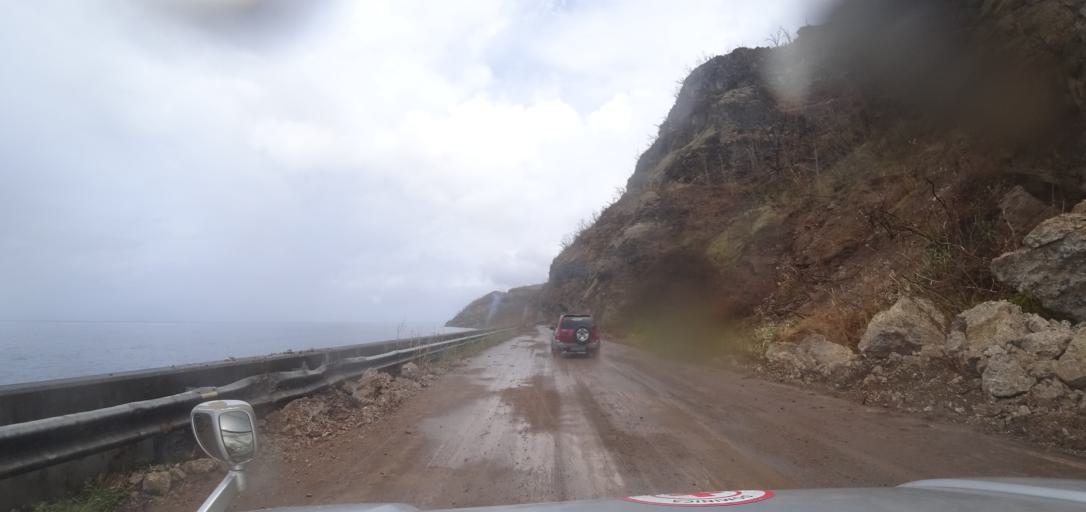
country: DM
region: Saint Peter
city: Colihaut
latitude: 15.4649
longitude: -61.4556
